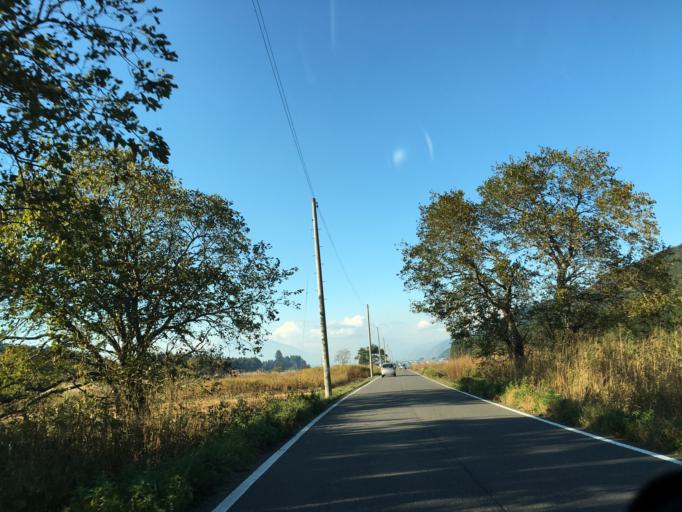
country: JP
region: Fukushima
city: Inawashiro
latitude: 37.4048
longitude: 140.1456
